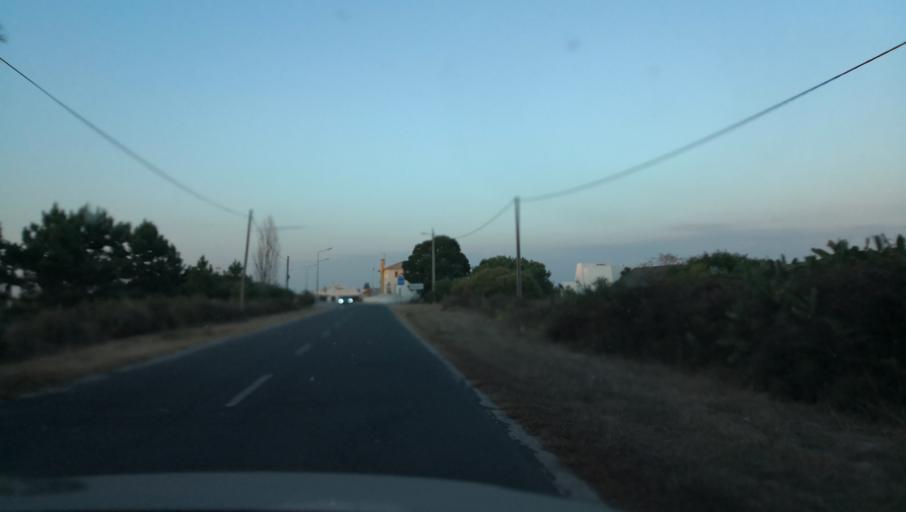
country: PT
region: Setubal
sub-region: Setubal
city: Setubal
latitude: 38.3927
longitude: -8.7790
